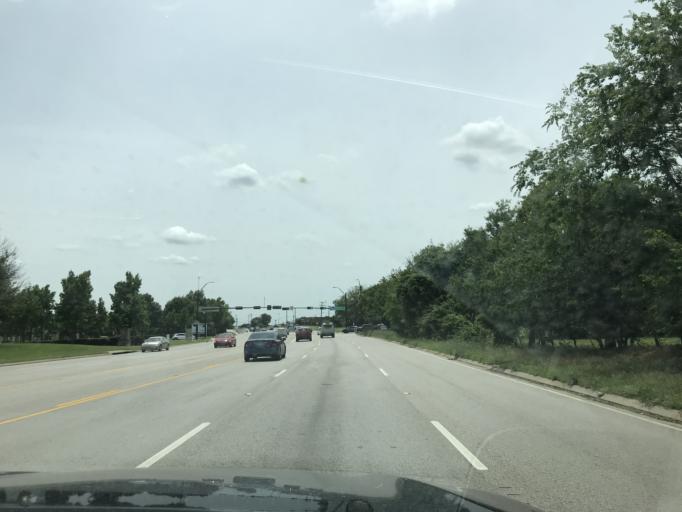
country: US
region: Texas
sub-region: Tarrant County
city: North Richland Hills
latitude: 32.8595
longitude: -97.2110
